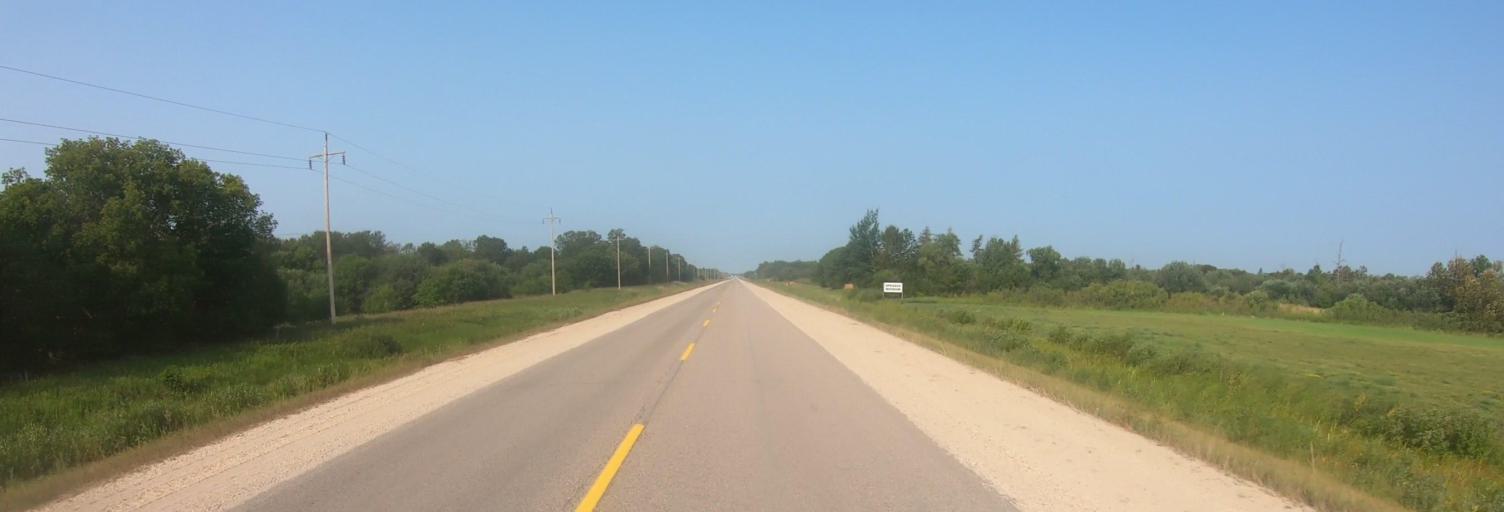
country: US
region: Minnesota
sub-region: Roseau County
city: Roseau
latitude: 49.0234
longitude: -95.6132
